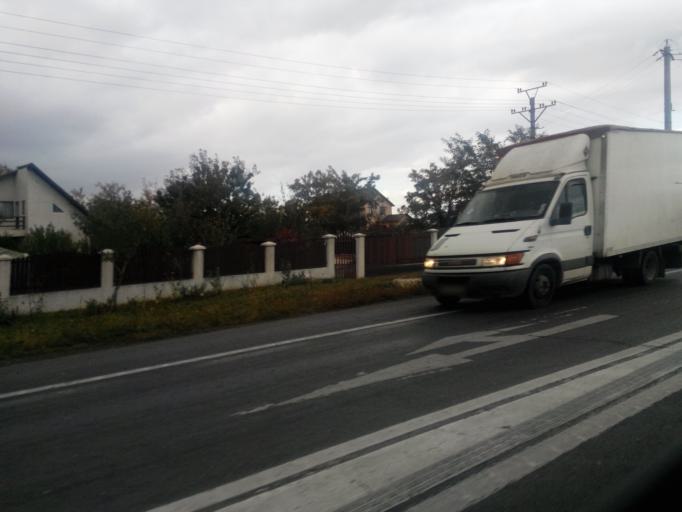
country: RO
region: Buzau
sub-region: Comuna Posta Calnau
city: Posta Calnau
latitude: 45.2378
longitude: 26.8736
